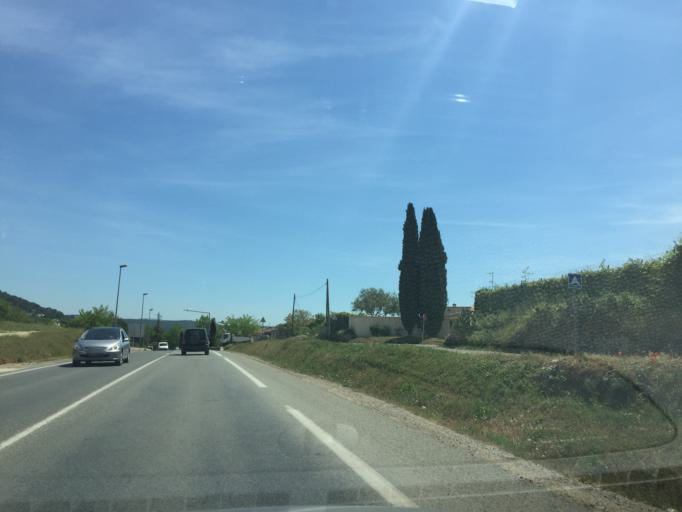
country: FR
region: Provence-Alpes-Cote d'Azur
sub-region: Departement du Var
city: Lorgues
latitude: 43.4892
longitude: 6.3556
